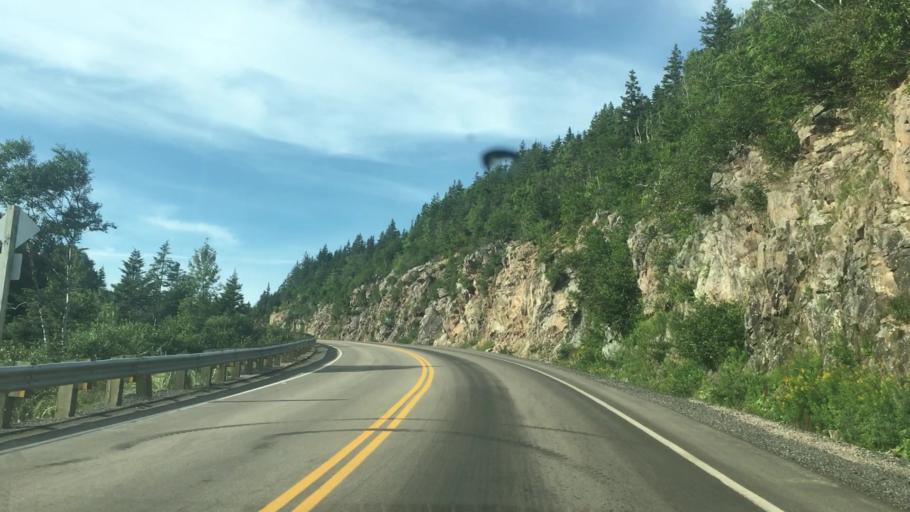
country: CA
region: Nova Scotia
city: Sydney Mines
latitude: 46.8216
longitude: -60.6544
